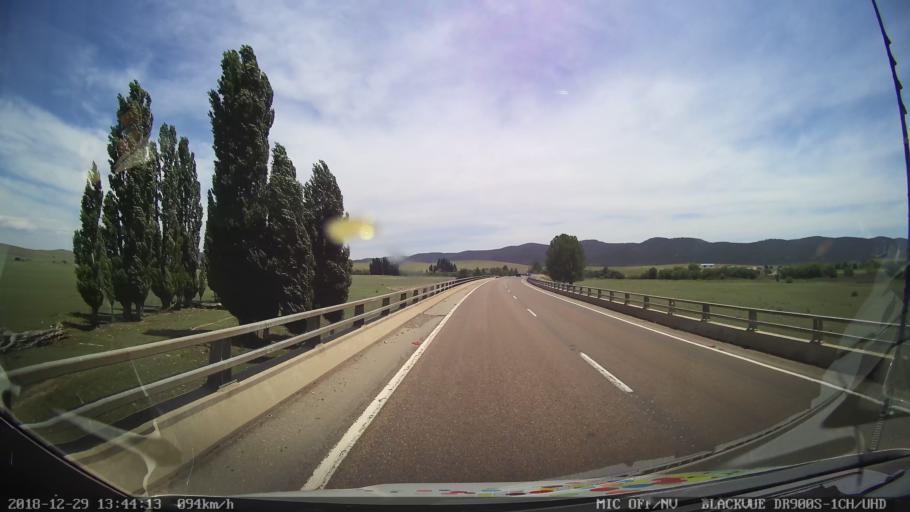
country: AU
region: New South Wales
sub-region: Cooma-Monaro
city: Cooma
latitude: -36.0824
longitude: 149.1557
